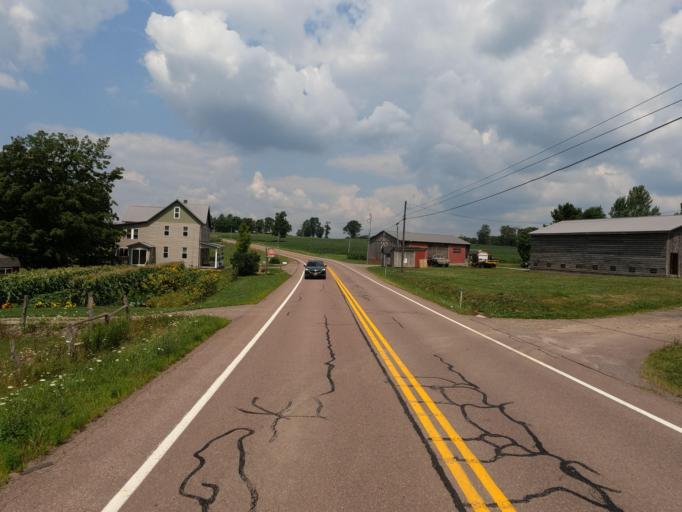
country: US
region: Maryland
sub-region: Allegany County
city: Westernport
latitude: 39.6157
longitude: -79.2150
